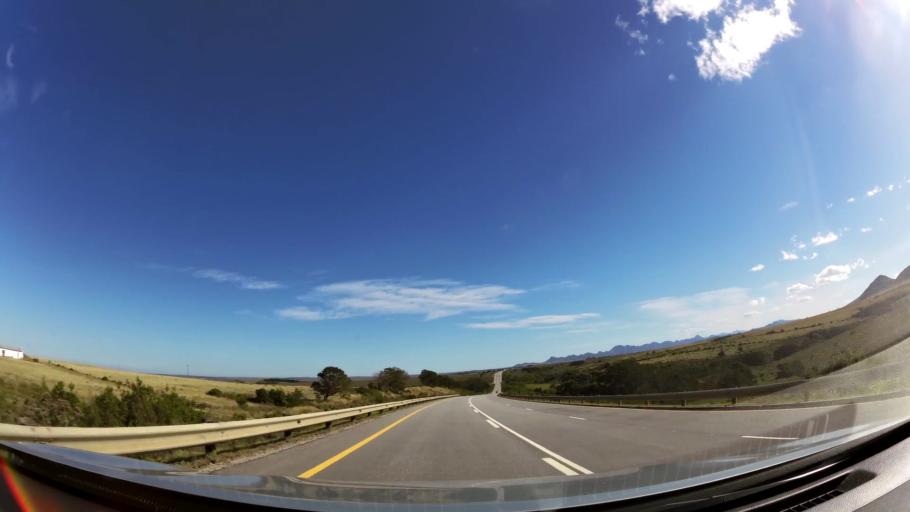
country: ZA
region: Eastern Cape
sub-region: Cacadu District Municipality
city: Kruisfontein
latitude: -34.0048
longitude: 24.6763
